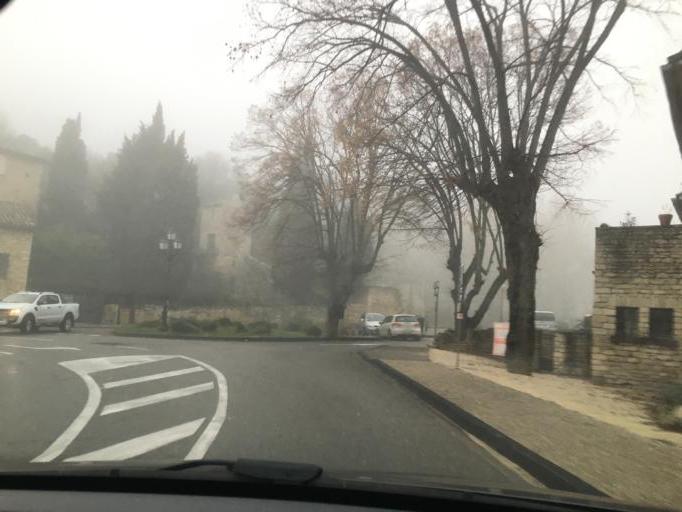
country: FR
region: Provence-Alpes-Cote d'Azur
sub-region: Departement du Vaucluse
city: Gordes
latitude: 43.9137
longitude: 5.1975
